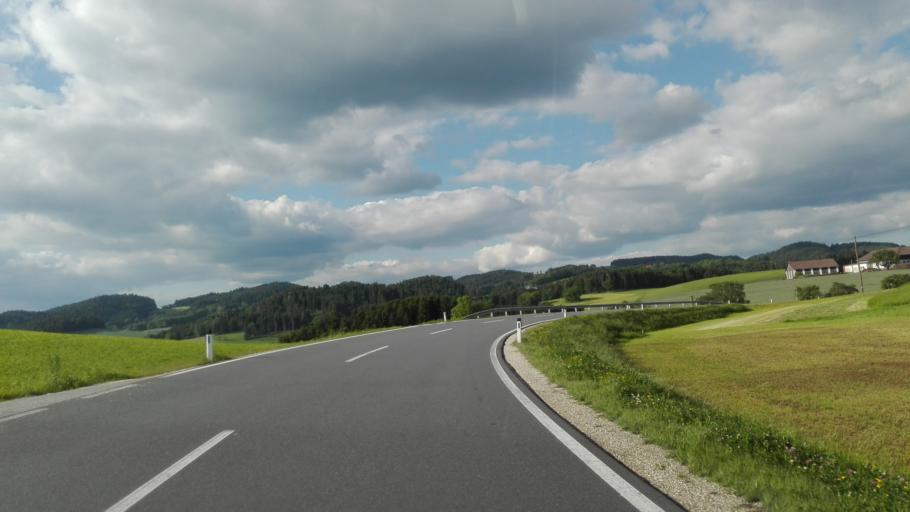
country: AT
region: Upper Austria
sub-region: Politischer Bezirk Perg
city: Perg
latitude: 48.3703
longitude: 14.6824
